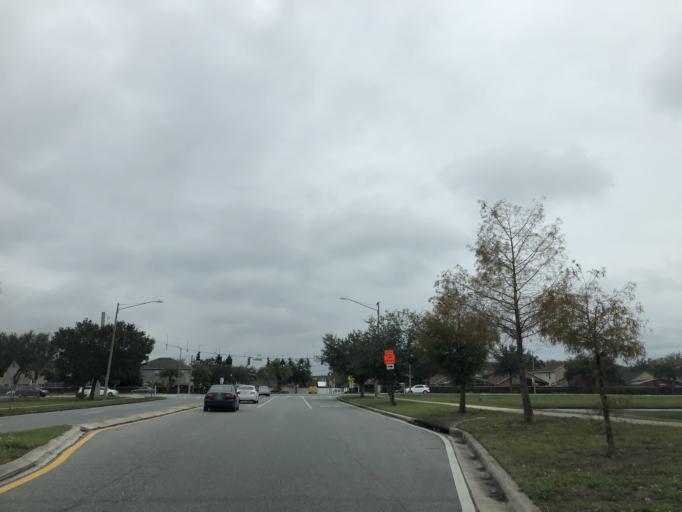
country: US
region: Florida
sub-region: Orange County
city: Hunters Creek
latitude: 28.3681
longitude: -81.3992
